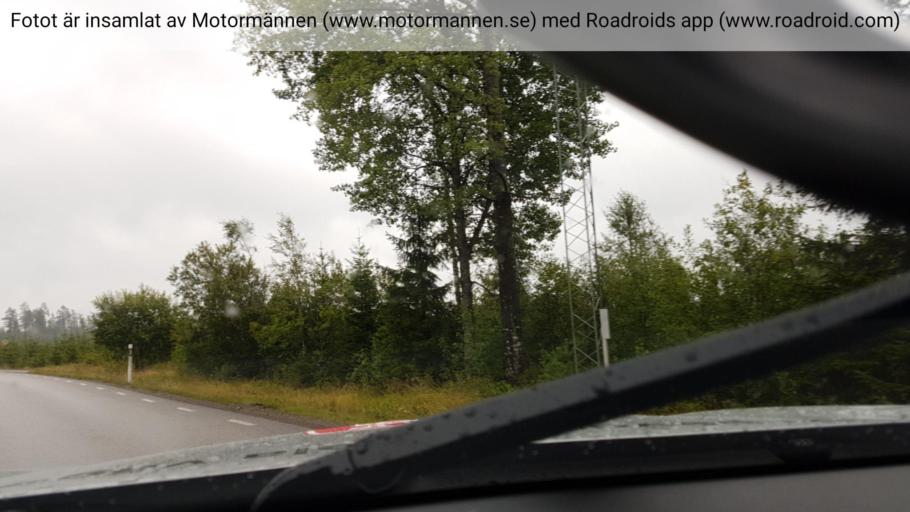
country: SE
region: Vaestra Goetaland
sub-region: Bengtsfors Kommun
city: Dals Langed
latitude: 58.8257
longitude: 12.1394
